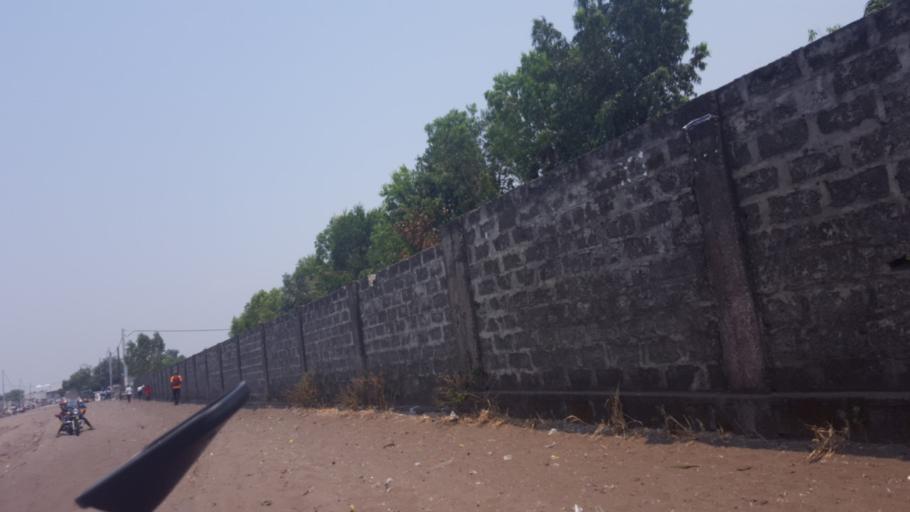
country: CD
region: Kinshasa
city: Masina
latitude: -4.3598
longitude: 15.5071
